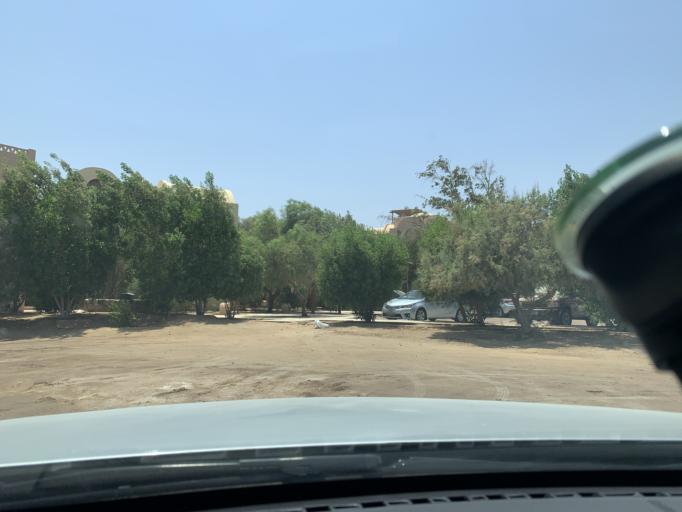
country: EG
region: Red Sea
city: El Gouna
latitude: 27.4004
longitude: 33.6748
